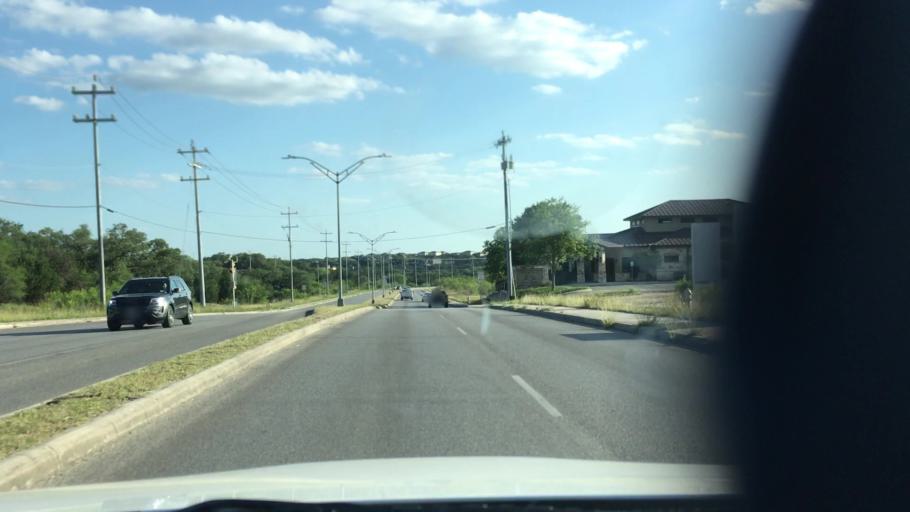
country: US
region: Texas
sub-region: Bexar County
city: Timberwood Park
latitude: 29.6578
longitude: -98.4388
